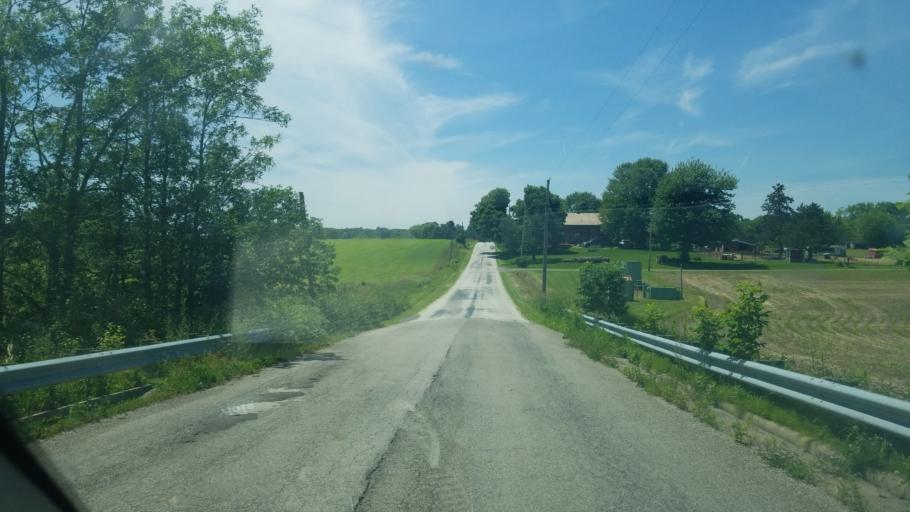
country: US
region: Ohio
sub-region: Stark County
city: Alliance
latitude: 40.8577
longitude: -81.0696
